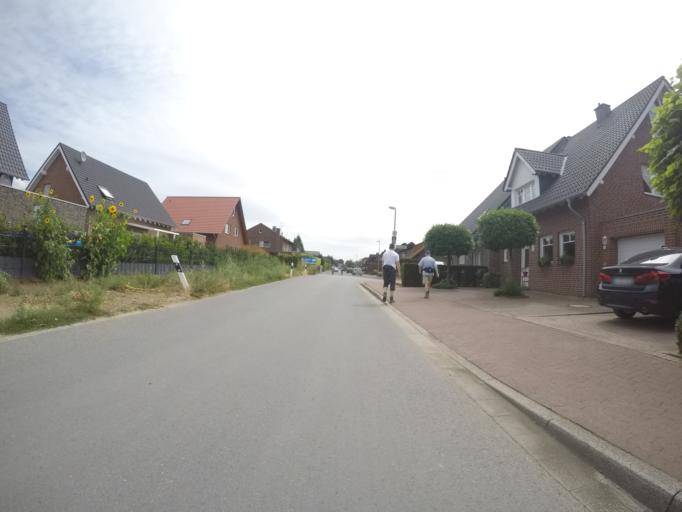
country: DE
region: North Rhine-Westphalia
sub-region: Regierungsbezirk Dusseldorf
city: Bocholt
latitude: 51.8530
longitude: 6.5872
